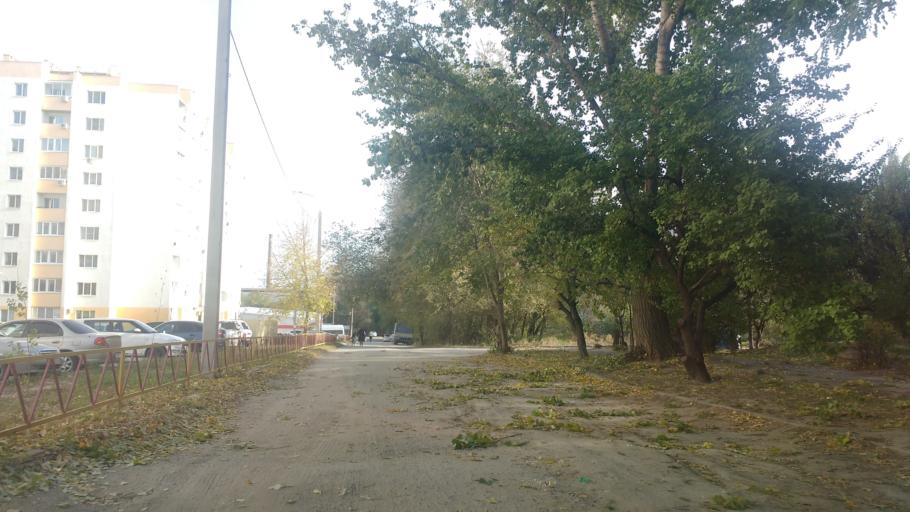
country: RU
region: Volgograd
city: Krasnoslobodsk
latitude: 48.7616
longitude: 44.5510
